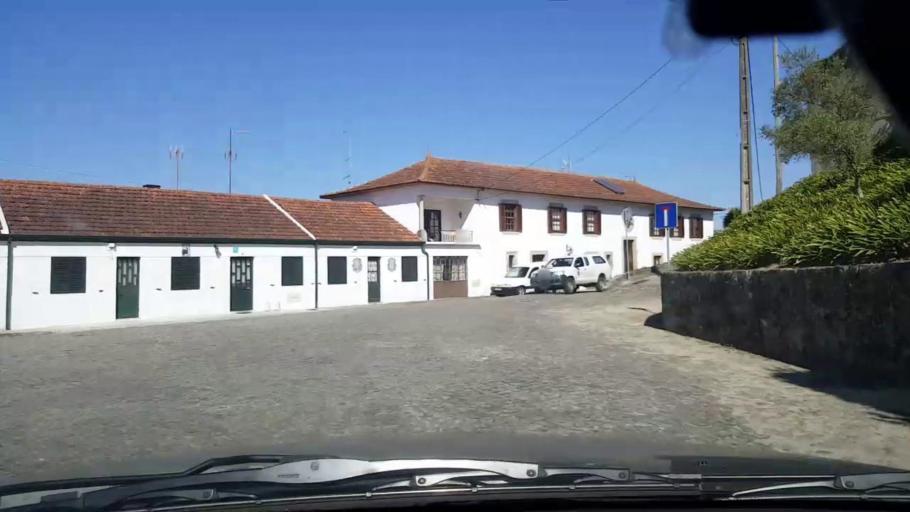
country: PT
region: Porto
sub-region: Vila do Conde
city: Arvore
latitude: 41.3330
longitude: -8.6689
